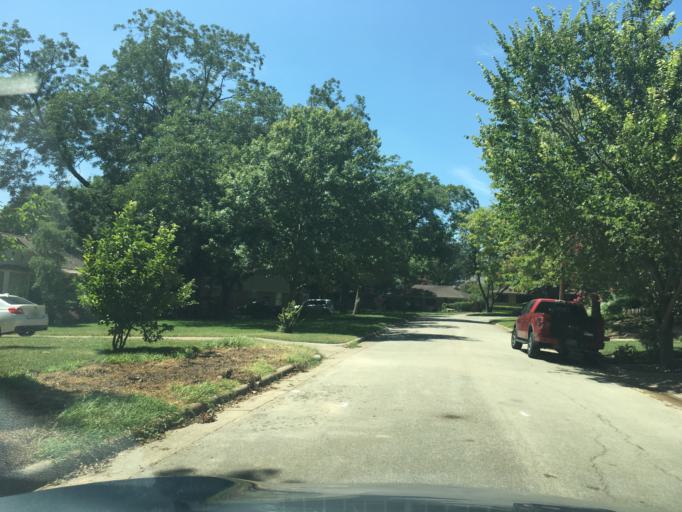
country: US
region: Texas
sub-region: Dallas County
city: Highland Park
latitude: 32.8645
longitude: -96.7294
